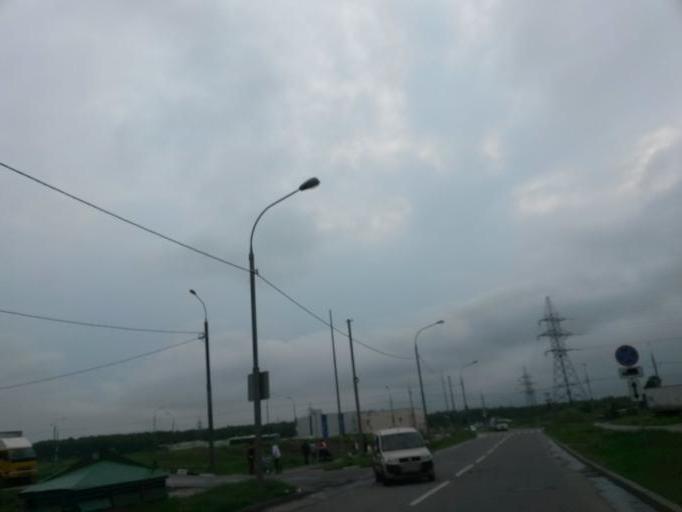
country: RU
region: Moskovskaya
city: Shcherbinka
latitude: 55.5010
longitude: 37.5949
